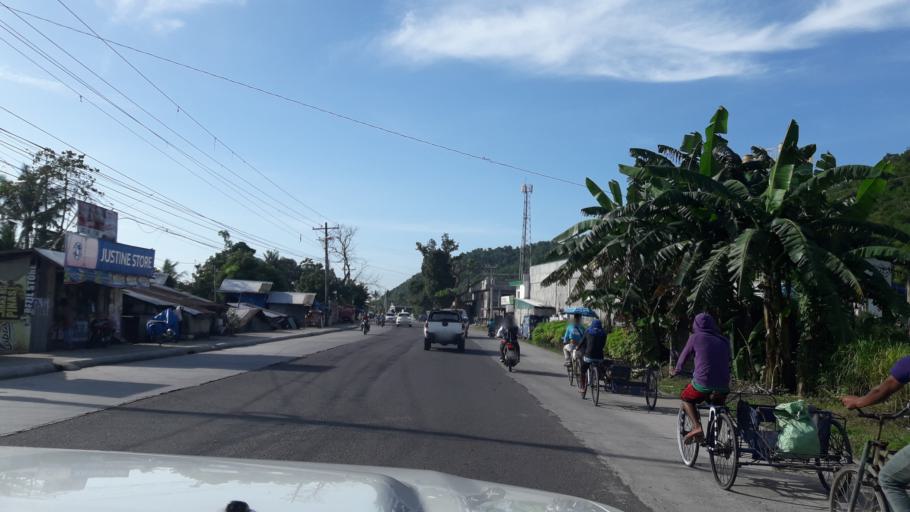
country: PH
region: Eastern Visayas
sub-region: Province of Leyte
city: Pawing
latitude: 11.1969
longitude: 124.9916
